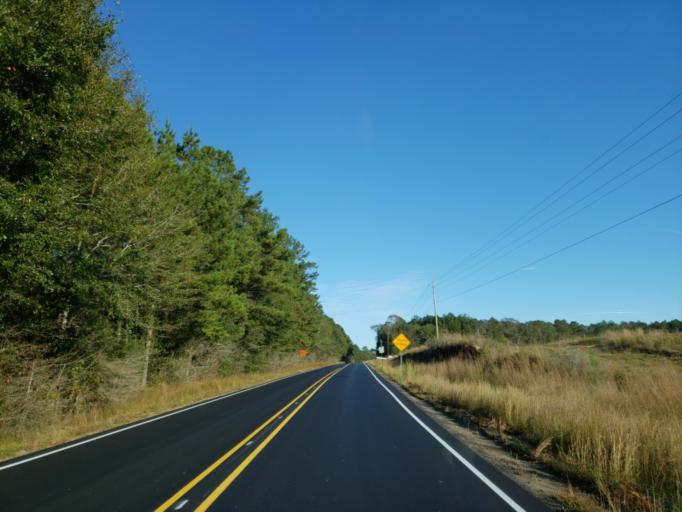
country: US
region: Mississippi
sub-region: Perry County
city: Richton
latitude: 31.3749
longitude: -88.8314
